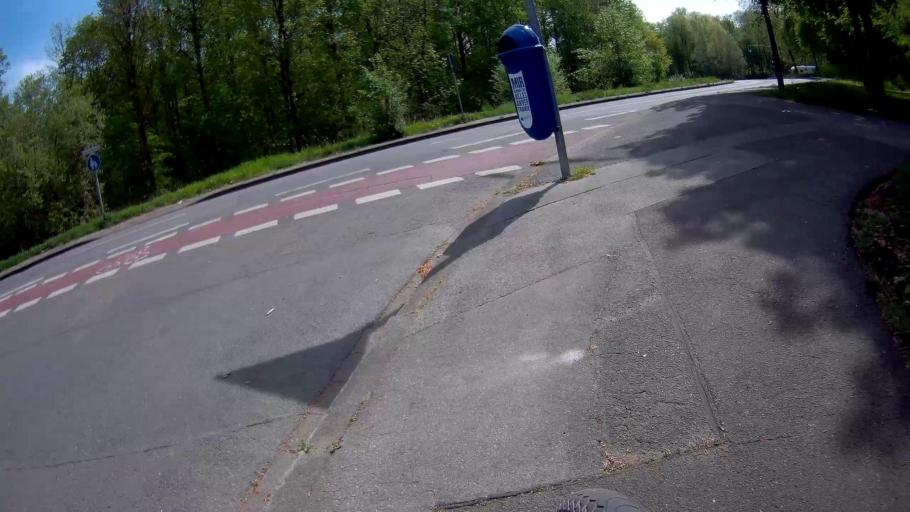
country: DE
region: North Rhine-Westphalia
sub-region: Regierungsbezirk Munster
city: Gelsenkirchen
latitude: 51.5556
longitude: 7.1056
